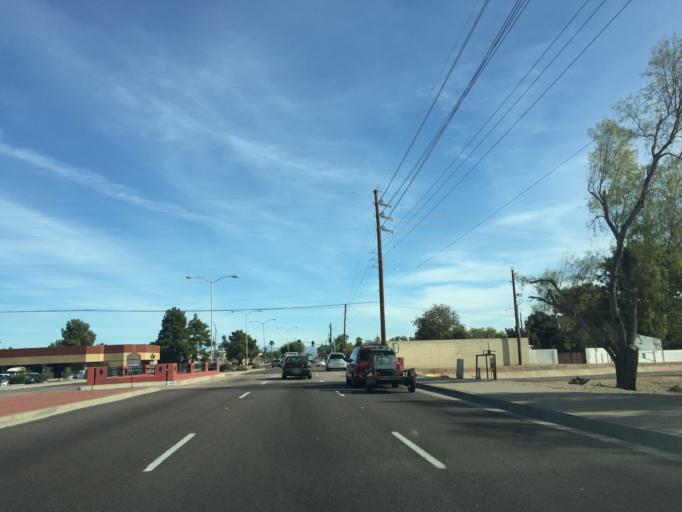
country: US
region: Arizona
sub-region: Maricopa County
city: Tempe
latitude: 33.4074
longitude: -111.8890
